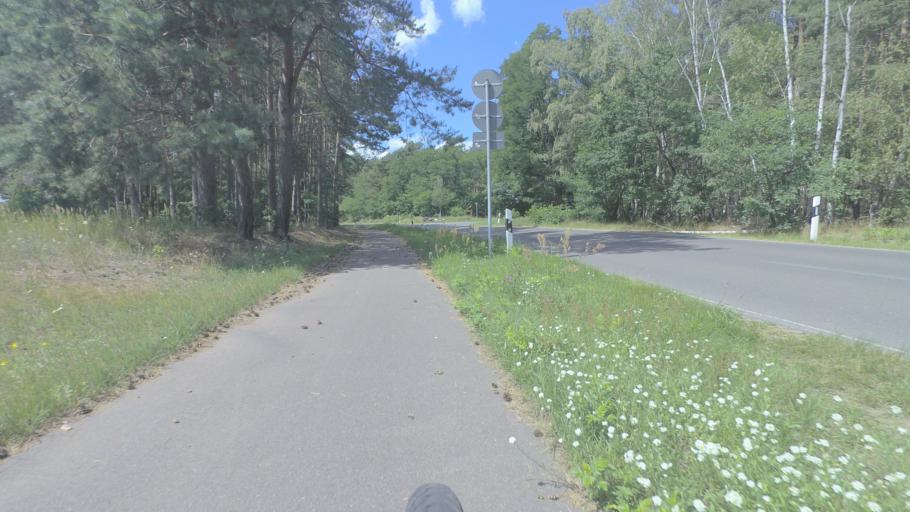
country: DE
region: Brandenburg
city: Trebbin
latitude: 52.1938
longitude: 13.1501
